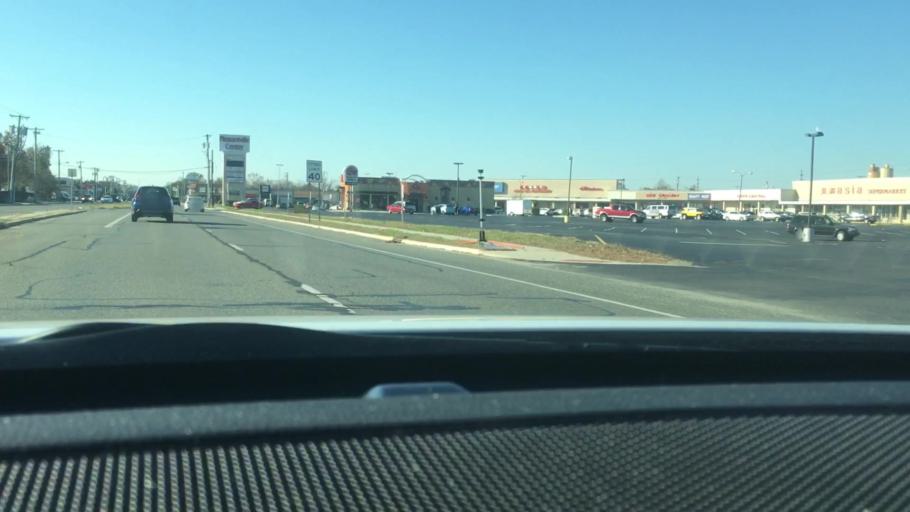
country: US
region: New Jersey
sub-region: Atlantic County
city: Pleasantville
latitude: 39.3930
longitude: -74.5362
